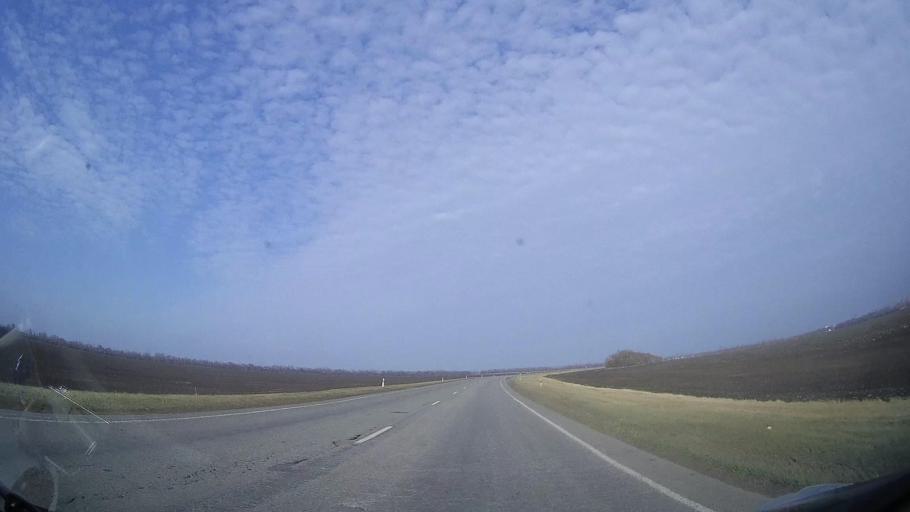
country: RU
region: Rostov
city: Tselina
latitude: 46.5169
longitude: 40.9953
